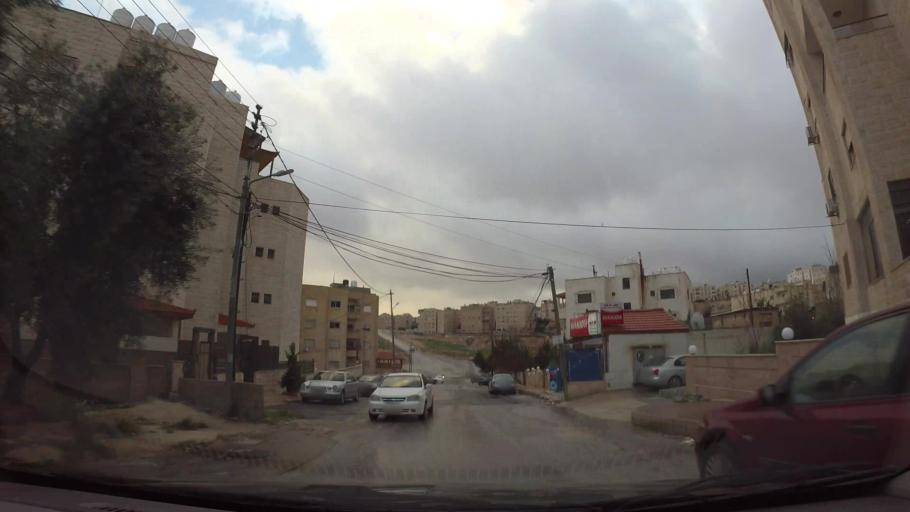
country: JO
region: Amman
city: Amman
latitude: 32.0025
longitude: 35.9300
